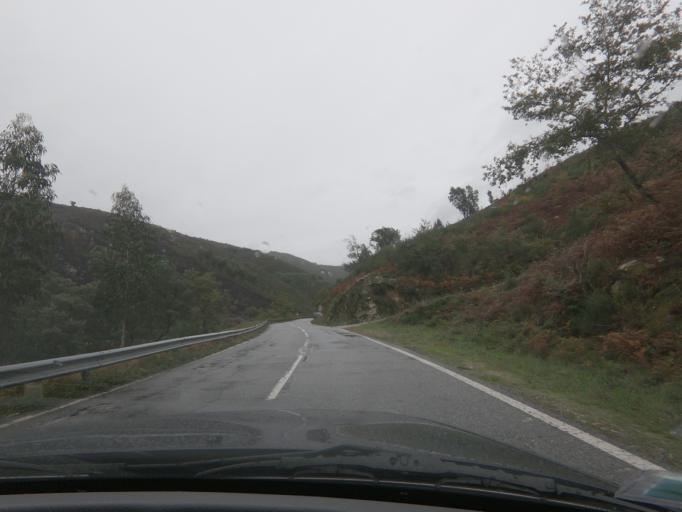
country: PT
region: Vila Real
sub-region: Mondim de Basto
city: Mondim de Basto
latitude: 41.3702
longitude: -7.9271
